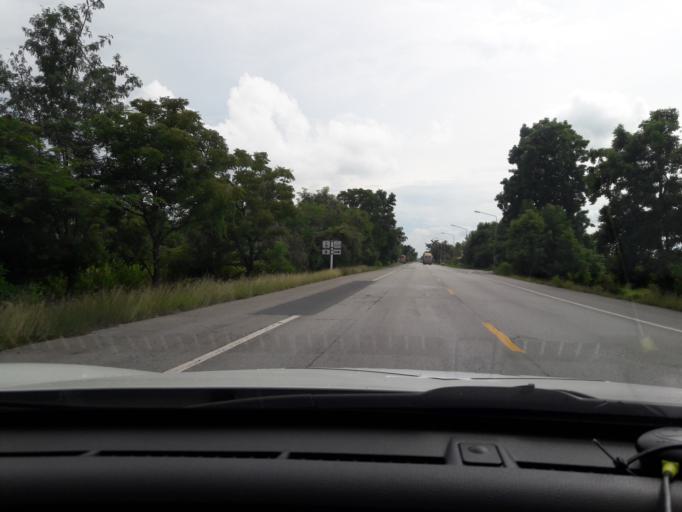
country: TH
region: Nakhon Sawan
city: Phai Sali
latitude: 15.5793
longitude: 100.5608
